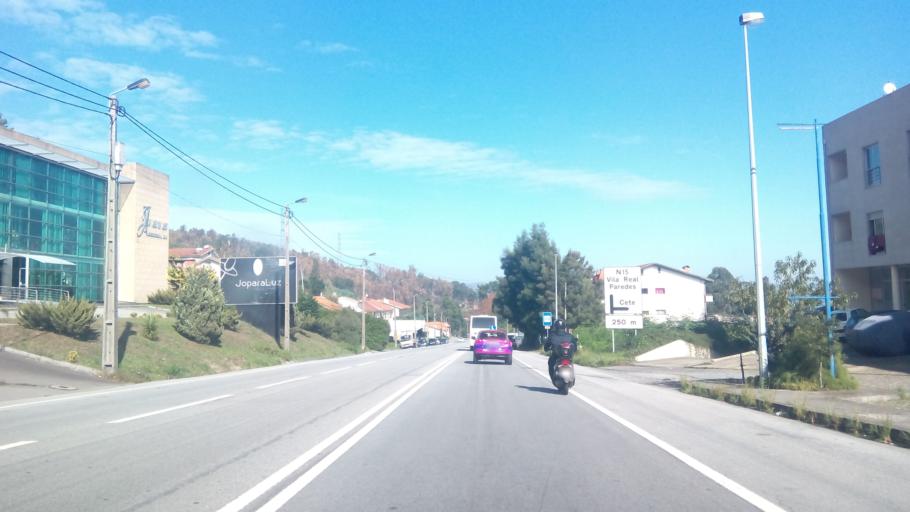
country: PT
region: Porto
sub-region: Paredes
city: Baltar
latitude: 41.1907
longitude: -8.3669
